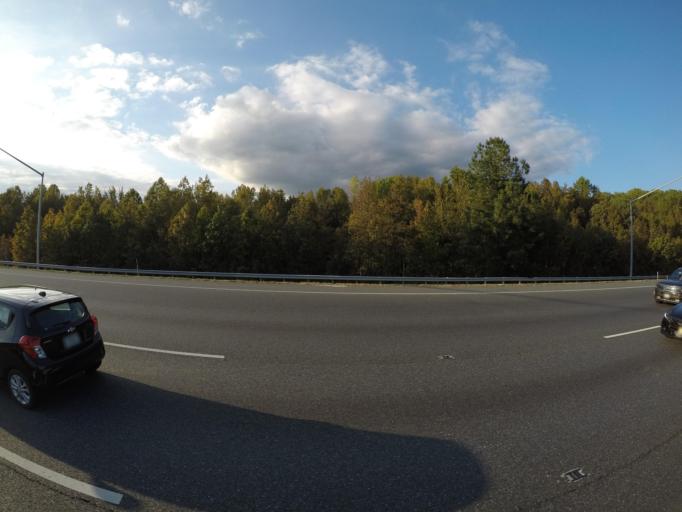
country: US
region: Maryland
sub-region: Harford County
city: Riverside
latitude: 39.4821
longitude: -76.2596
